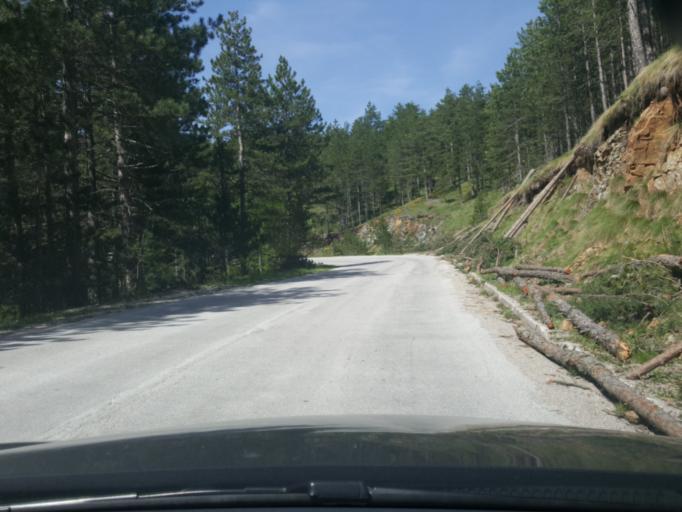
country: RS
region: Central Serbia
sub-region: Zlatiborski Okrug
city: Bajina Basta
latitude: 43.8777
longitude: 19.5659
